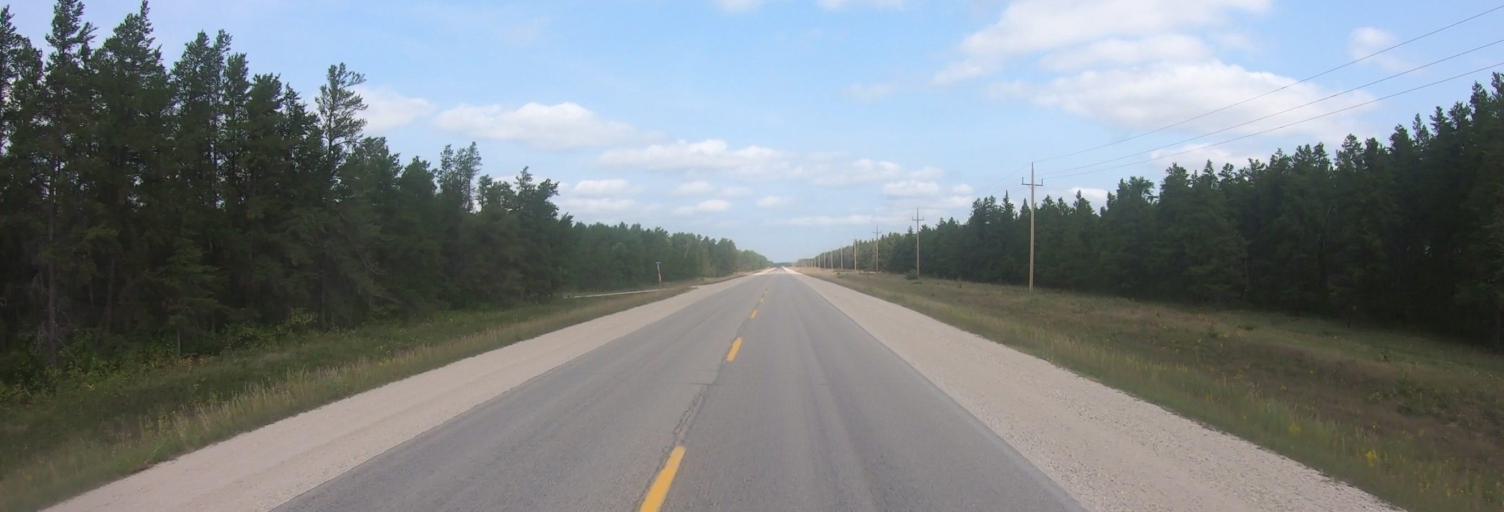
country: CA
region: Manitoba
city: La Broquerie
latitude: 49.2443
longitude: -96.3506
